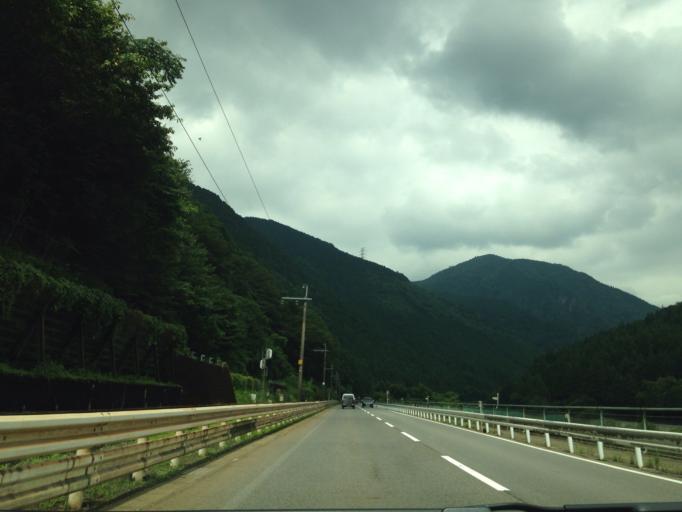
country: JP
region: Gifu
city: Mitake
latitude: 35.5811
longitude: 137.1811
